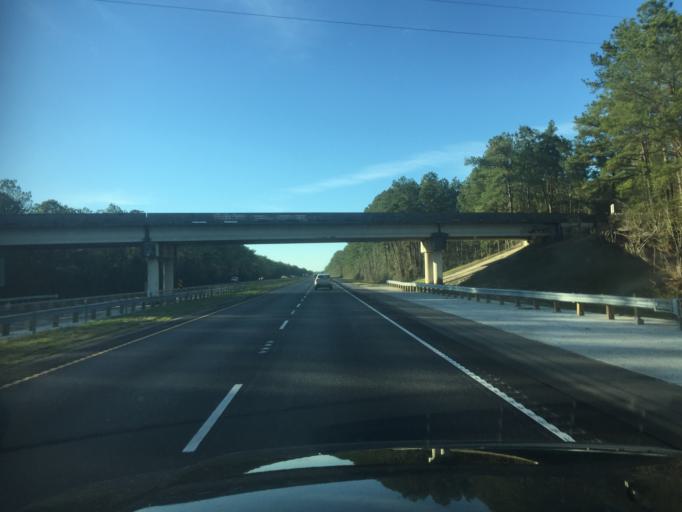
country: US
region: Louisiana
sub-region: Saint Tammany Parish
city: Lacombe
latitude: 30.3613
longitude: -89.9373
